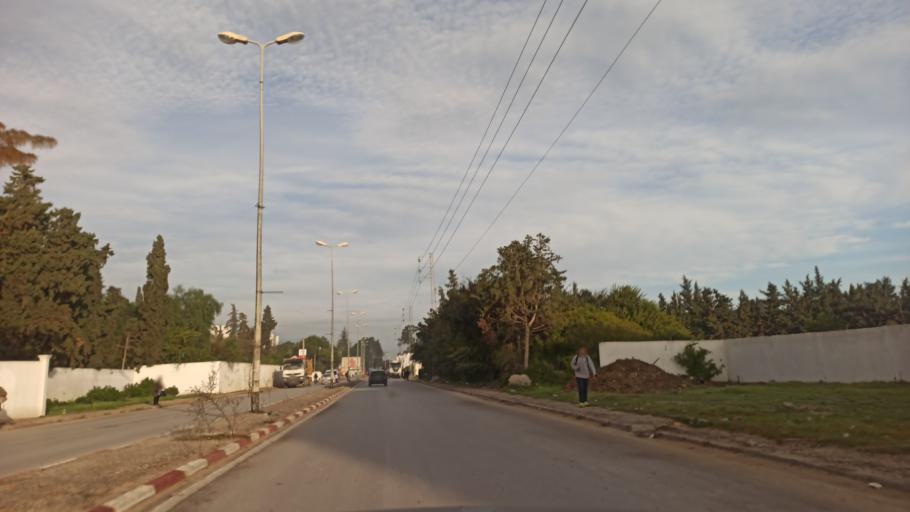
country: TN
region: Ariana
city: Ariana
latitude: 36.8731
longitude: 10.2470
